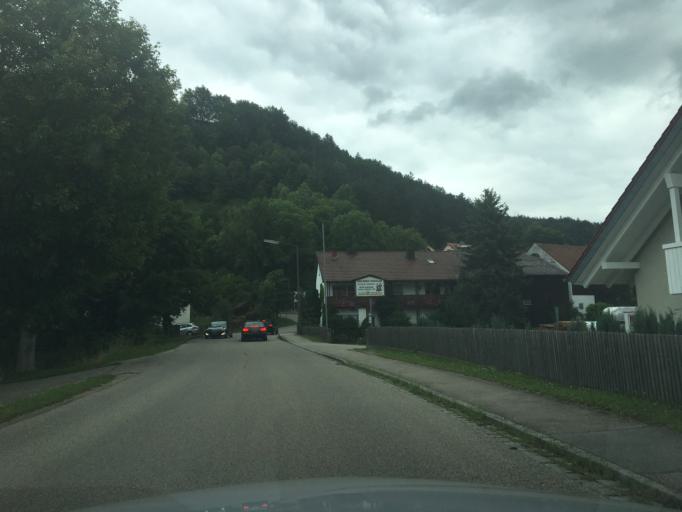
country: DE
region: Bavaria
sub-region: Regierungsbezirk Mittelfranken
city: Greding
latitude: 49.0002
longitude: 11.3790
